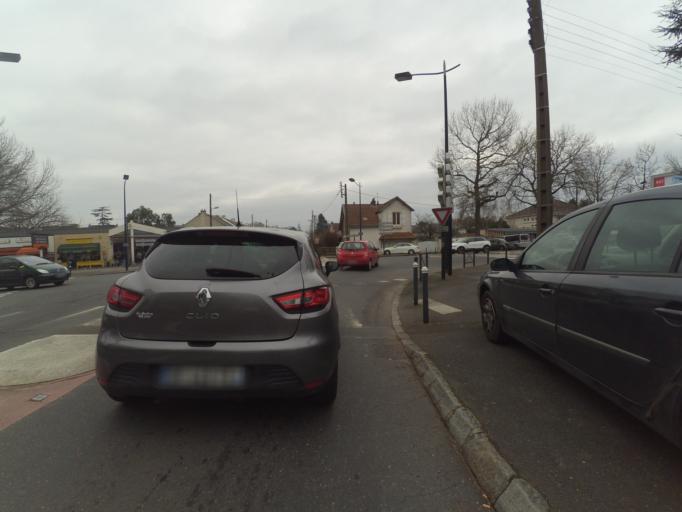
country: FR
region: Pays de la Loire
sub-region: Departement de la Loire-Atlantique
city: Bouguenais
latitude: 47.2183
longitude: -1.6042
